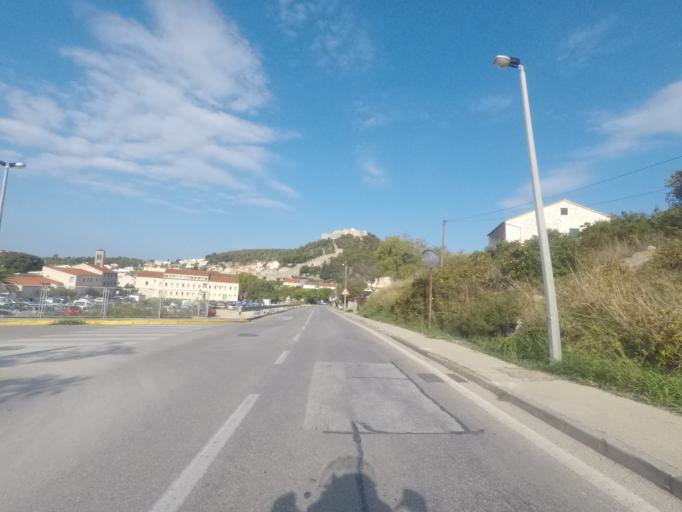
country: HR
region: Splitsko-Dalmatinska
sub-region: Grad Hvar
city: Hvar
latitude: 43.1725
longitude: 16.4472
